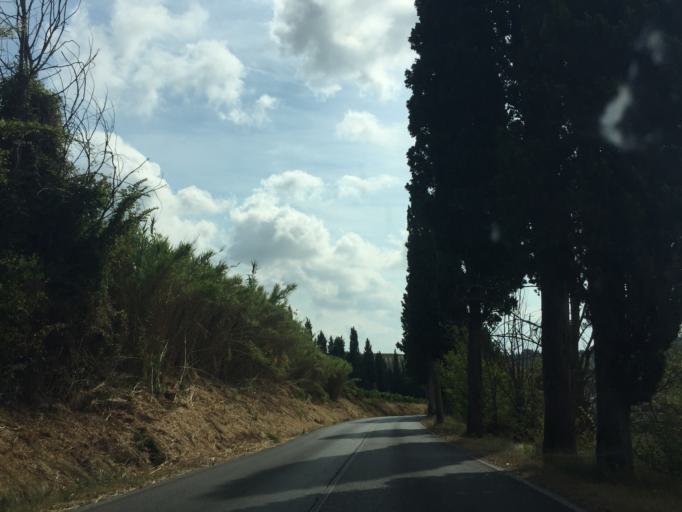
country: IT
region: Tuscany
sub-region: Province of Florence
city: Cerreto Guidi
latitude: 43.7454
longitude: 10.8961
